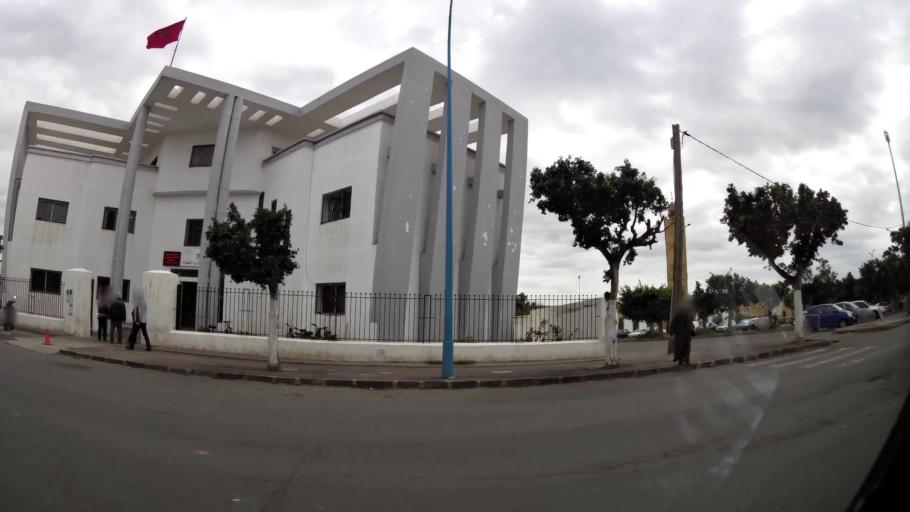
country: MA
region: Grand Casablanca
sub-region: Casablanca
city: Casablanca
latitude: 33.5743
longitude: -7.5729
